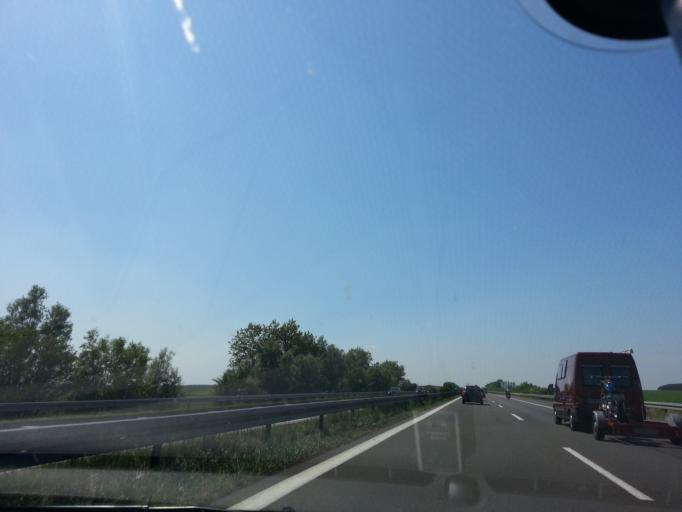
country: DE
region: Mecklenburg-Vorpommern
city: Spornitz
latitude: 53.3684
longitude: 11.7019
